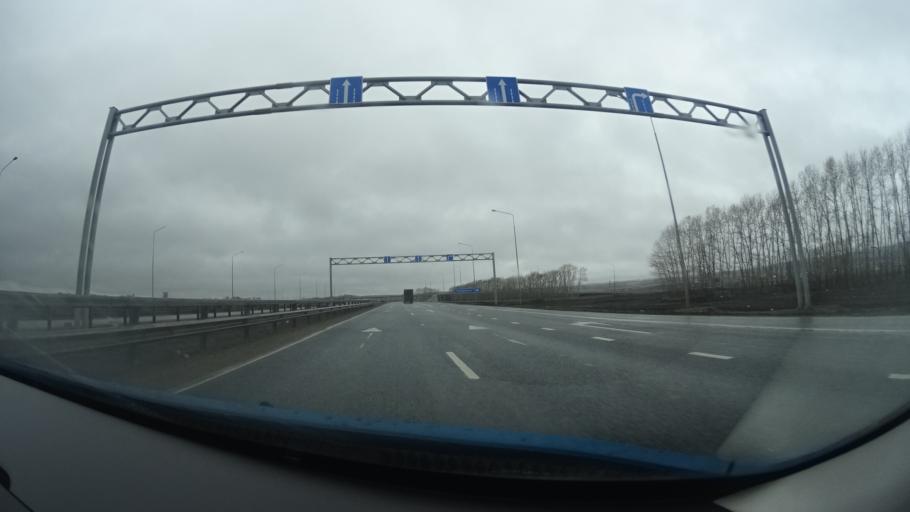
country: RU
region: Bashkortostan
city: Alekseyevka
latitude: 54.7249
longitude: 54.9282
